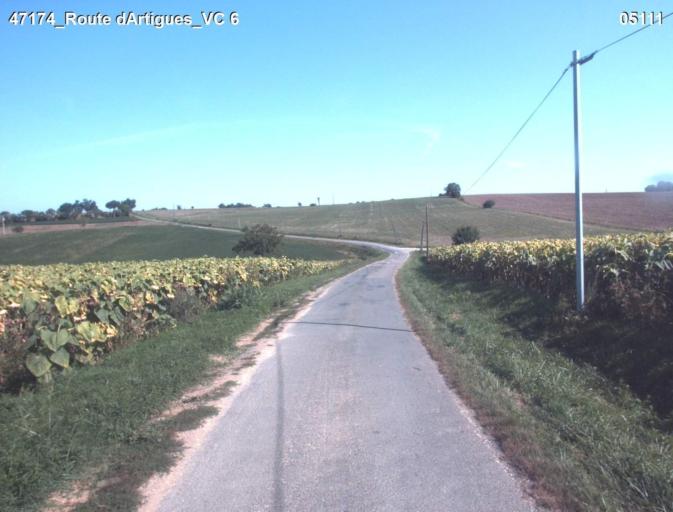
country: FR
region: Aquitaine
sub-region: Departement du Lot-et-Garonne
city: Mezin
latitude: 44.0449
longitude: 0.3340
